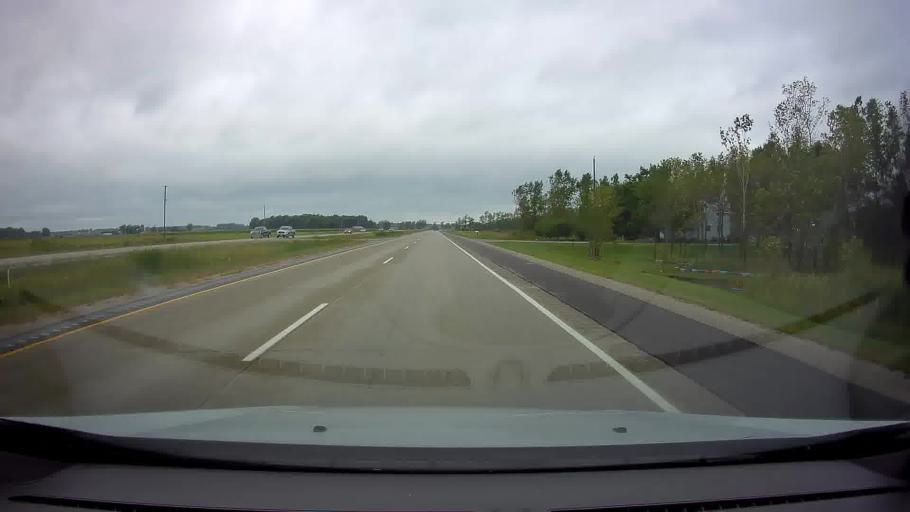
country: US
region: Wisconsin
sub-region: Brown County
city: Pulaski
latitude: 44.6105
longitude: -88.2591
